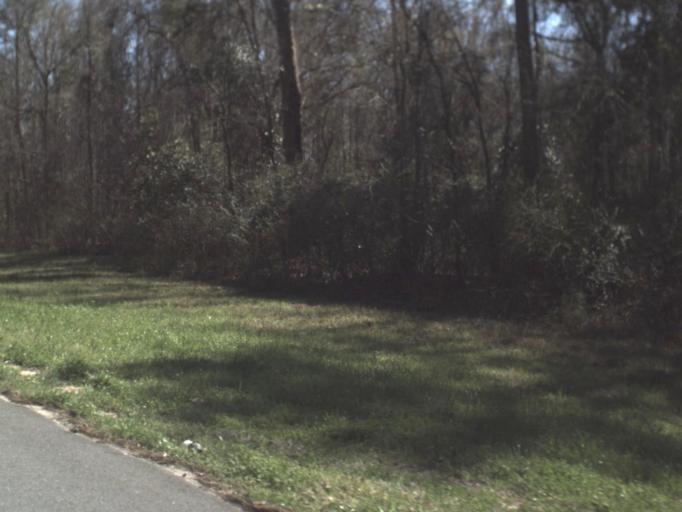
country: US
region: Florida
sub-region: Gadsden County
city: Gretna
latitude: 30.6865
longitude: -84.7189
